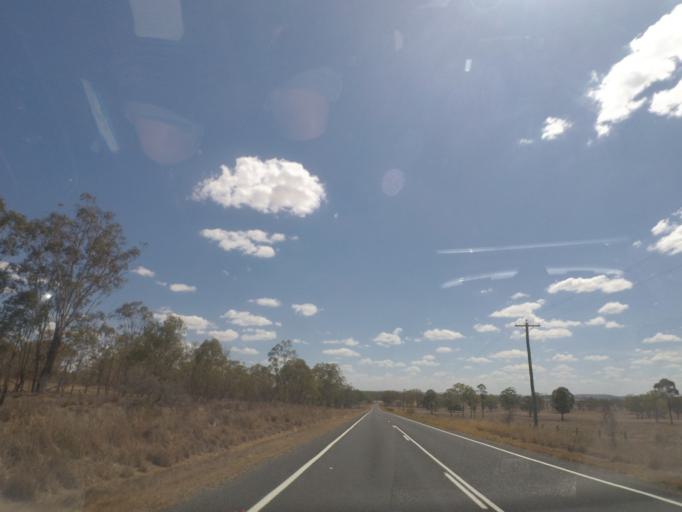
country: AU
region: Queensland
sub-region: Southern Downs
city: Warwick
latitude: -28.1800
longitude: 151.8231
